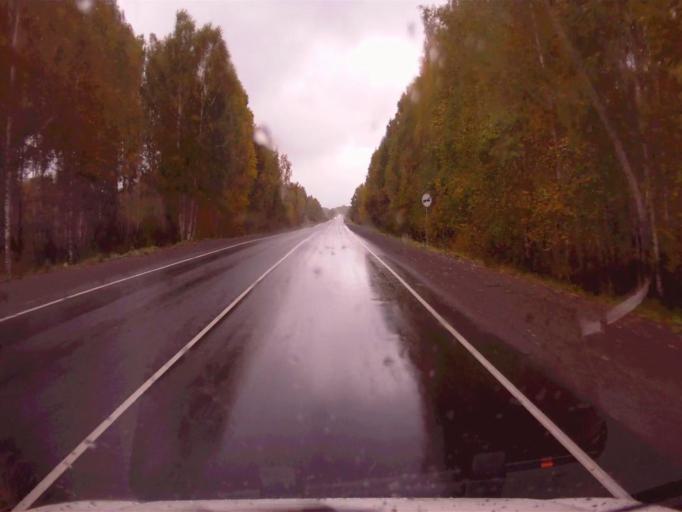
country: RU
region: Chelyabinsk
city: Argayash
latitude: 55.4791
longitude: 60.7598
